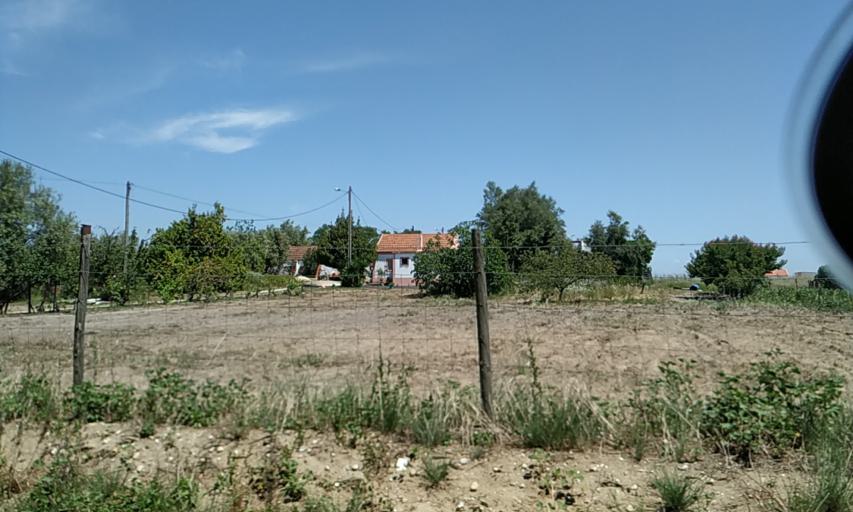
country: PT
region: Santarem
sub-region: Benavente
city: Poceirao
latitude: 38.6848
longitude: -8.7316
